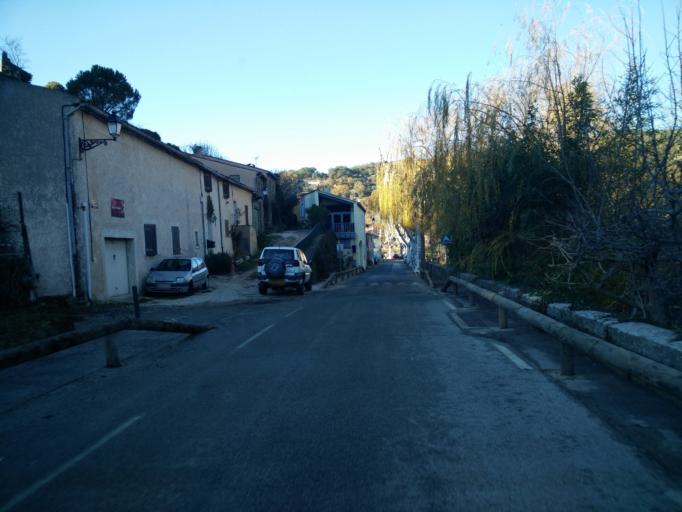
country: FR
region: Provence-Alpes-Cote d'Azur
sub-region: Departement du Var
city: Collobrieres
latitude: 43.2372
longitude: 6.3125
